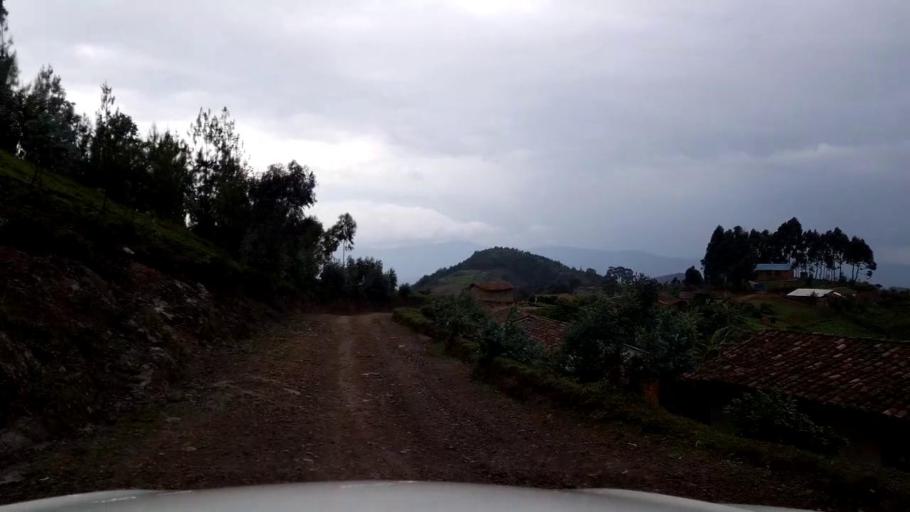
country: RW
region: Western Province
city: Kibuye
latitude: -2.0142
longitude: 29.4683
